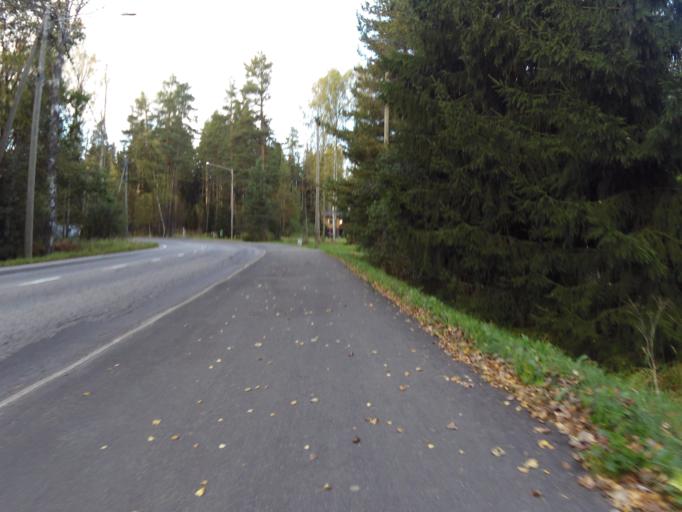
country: FI
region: Uusimaa
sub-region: Helsinki
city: Kauniainen
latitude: 60.2928
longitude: 24.7436
